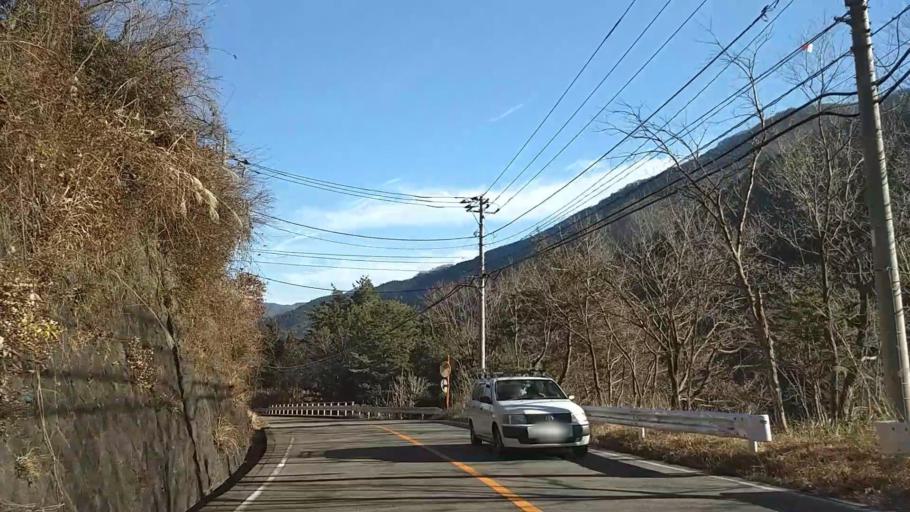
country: JP
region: Yamanashi
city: Uenohara
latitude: 35.5342
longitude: 139.0646
